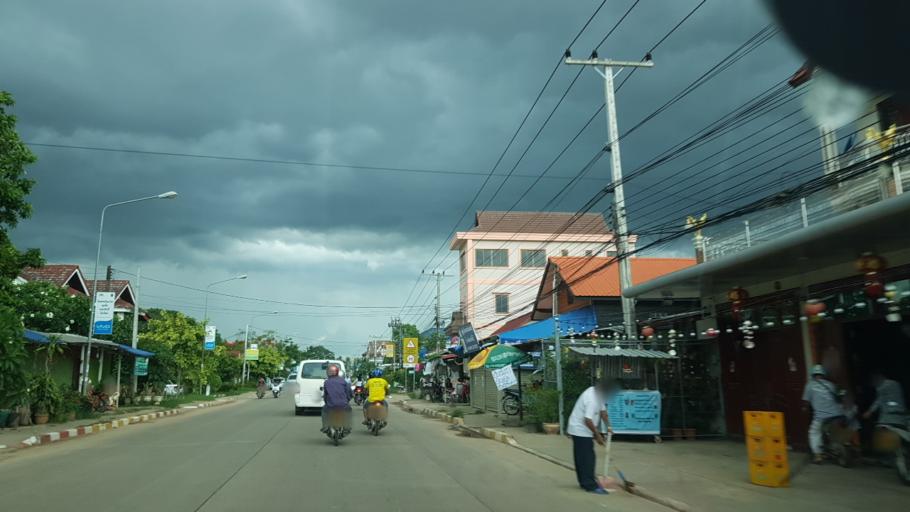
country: TH
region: Nong Khai
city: Si Chiang Mai
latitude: 17.9767
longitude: 102.5418
